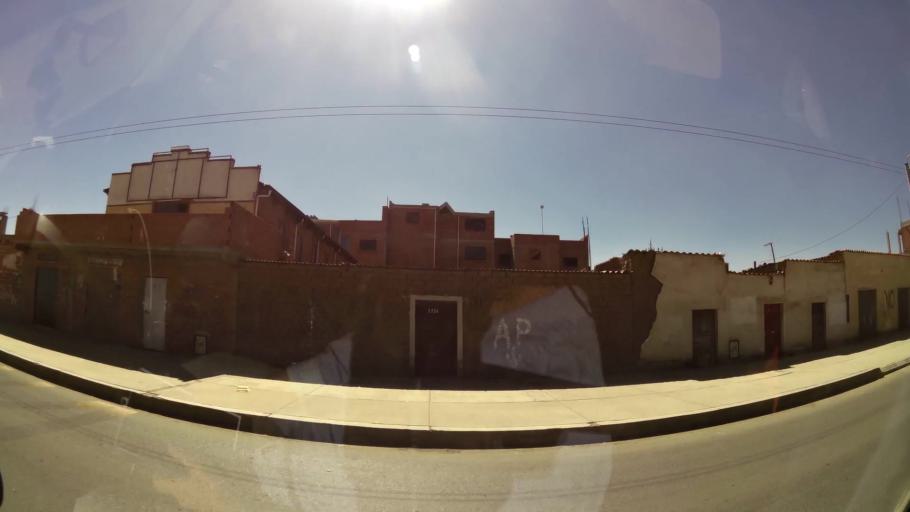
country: BO
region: La Paz
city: La Paz
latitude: -16.5337
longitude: -68.2080
